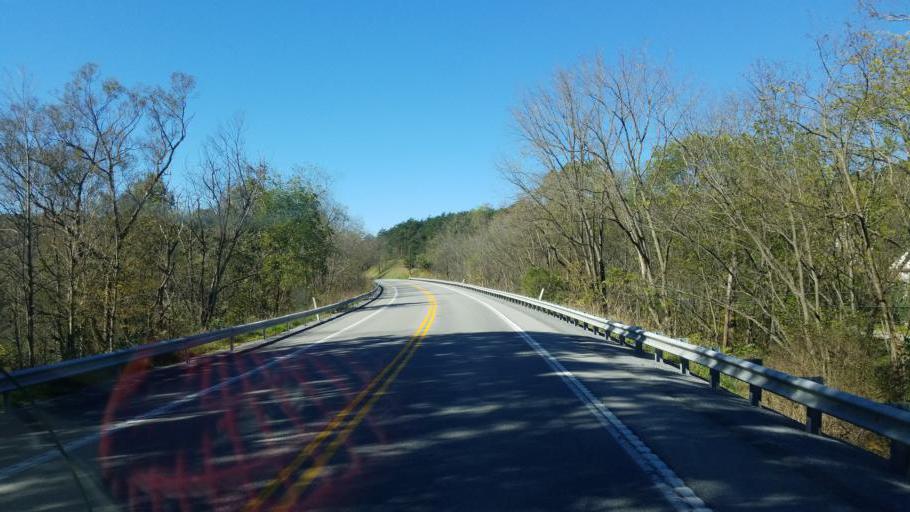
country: US
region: Pennsylvania
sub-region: Bedford County
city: Bedford
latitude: 40.0520
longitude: -78.6092
